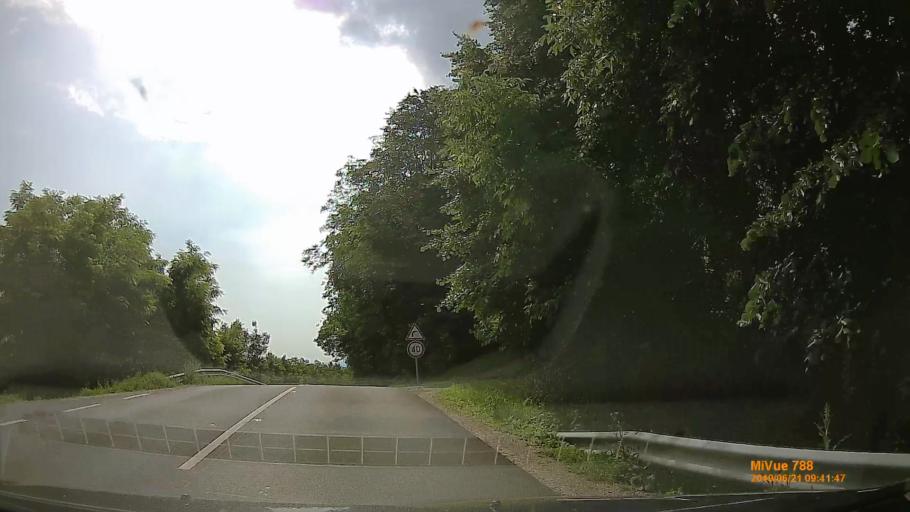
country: HU
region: Somogy
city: Taszar
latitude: 46.2929
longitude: 17.9618
